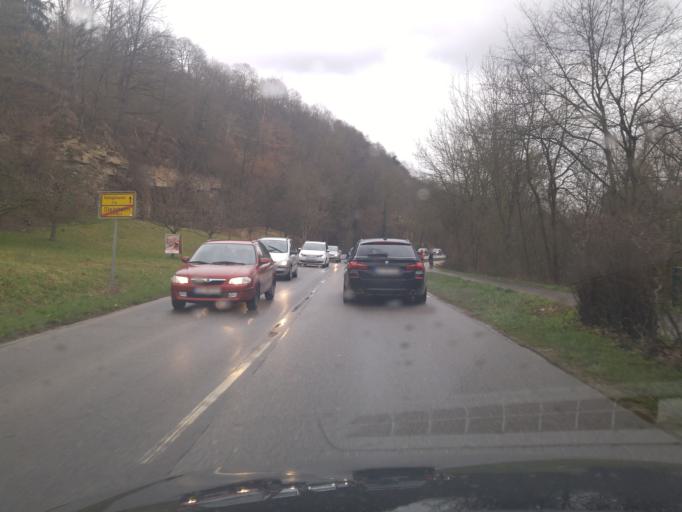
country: DE
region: Baden-Wuerttemberg
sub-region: Regierungsbezirk Stuttgart
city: Steinheim am der Murr
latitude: 48.9623
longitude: 9.2865
